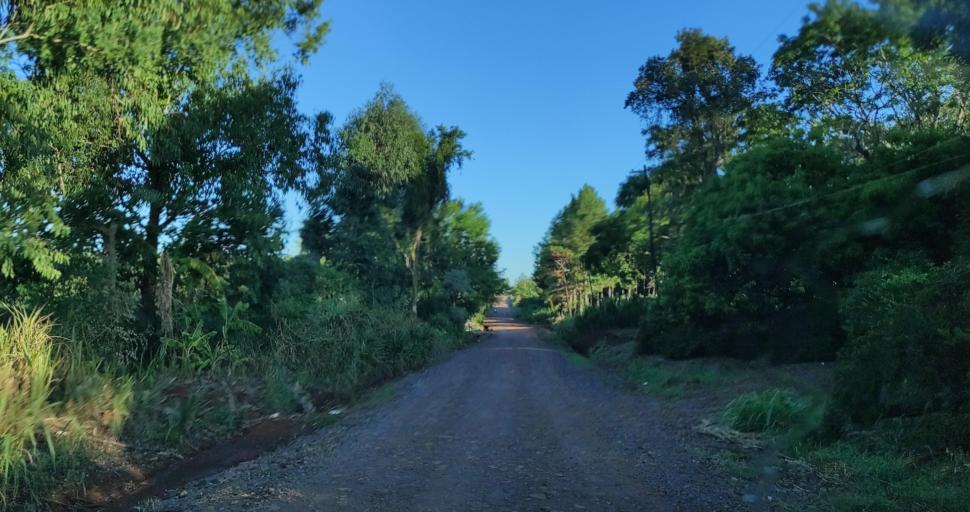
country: AR
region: Misiones
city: Gobernador Roca
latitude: -27.1991
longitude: -55.4626
